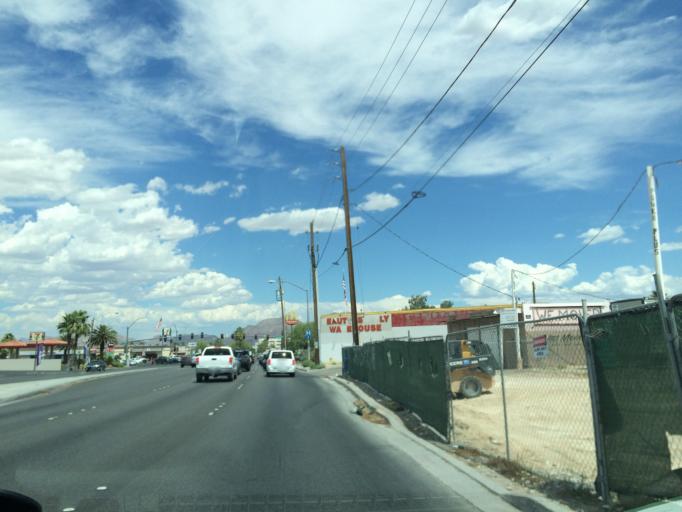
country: US
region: Nevada
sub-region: Clark County
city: North Las Vegas
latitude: 36.1958
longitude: -115.1308
